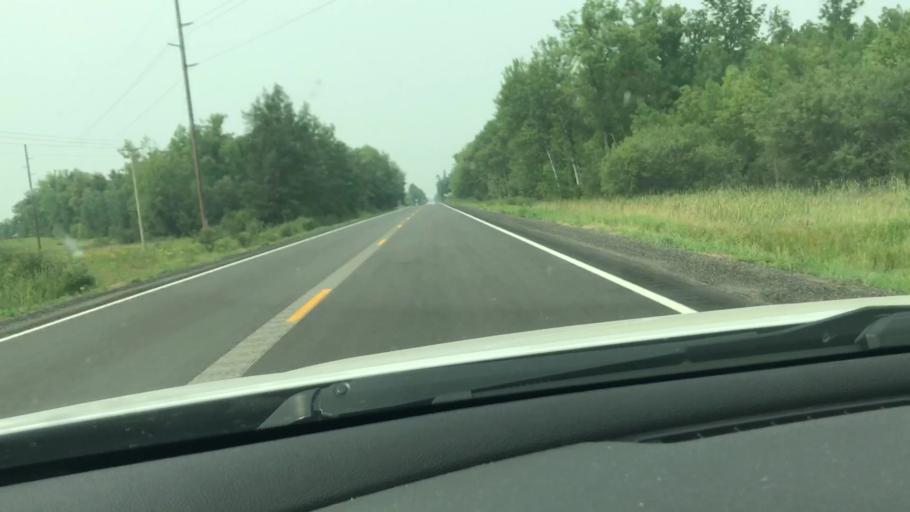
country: US
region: Minnesota
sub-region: Itasca County
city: Cohasset
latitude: 47.3648
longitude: -93.8735
